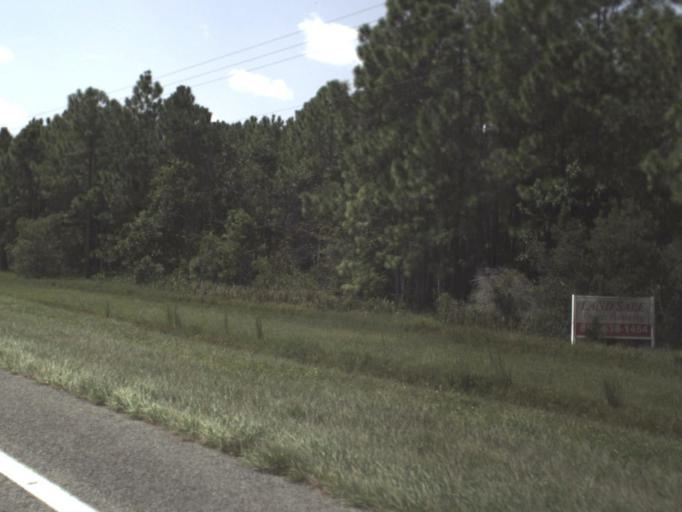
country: US
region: Florida
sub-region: Polk County
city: Crooked Lake Park
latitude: 27.7731
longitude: -81.5973
